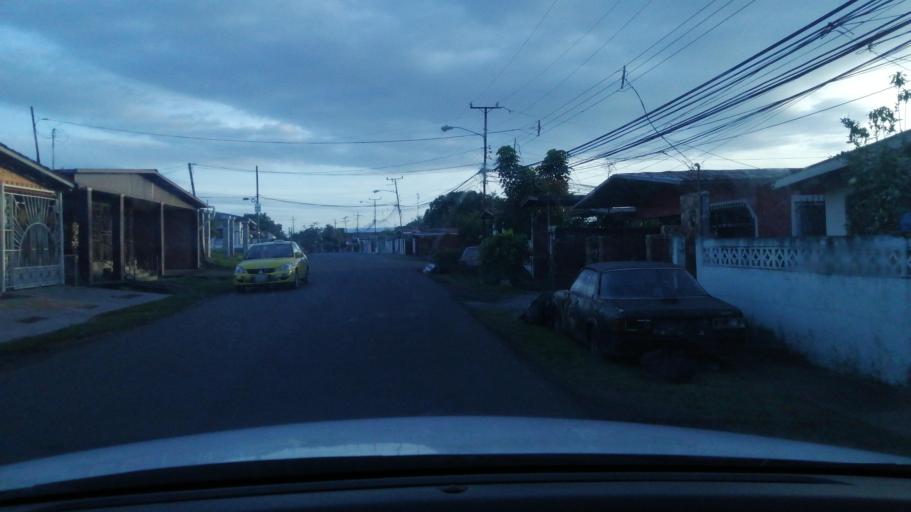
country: PA
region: Chiriqui
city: David
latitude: 8.4098
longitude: -82.4335
